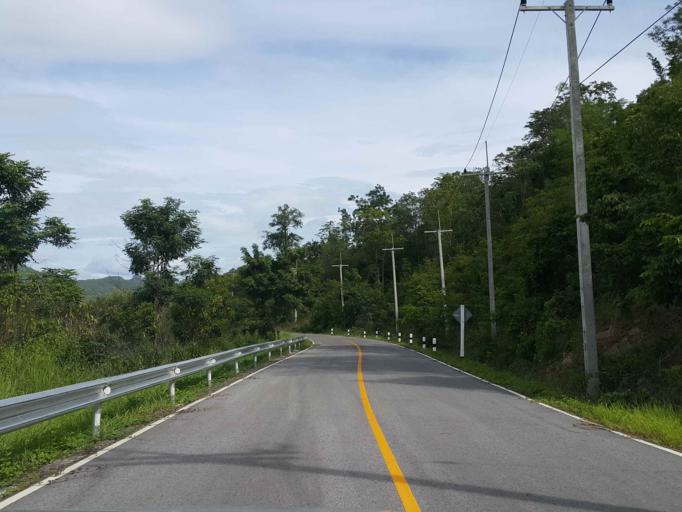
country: TH
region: Sukhothai
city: Thung Saliam
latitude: 17.2406
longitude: 99.4955
